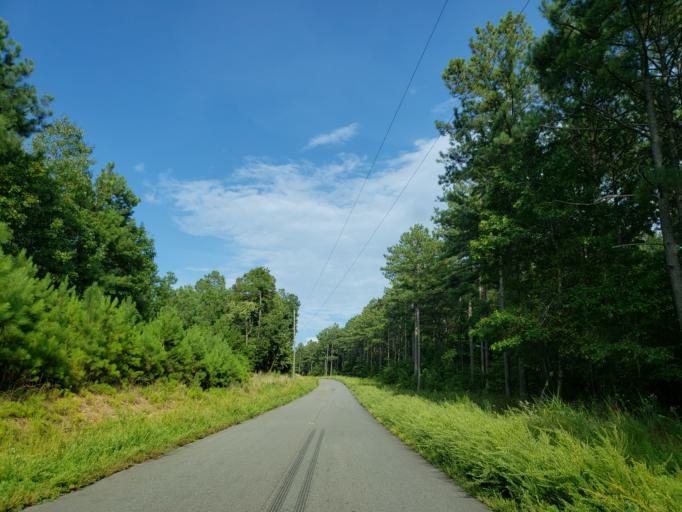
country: US
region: Georgia
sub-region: Bartow County
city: Emerson
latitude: 34.1906
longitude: -84.6560
